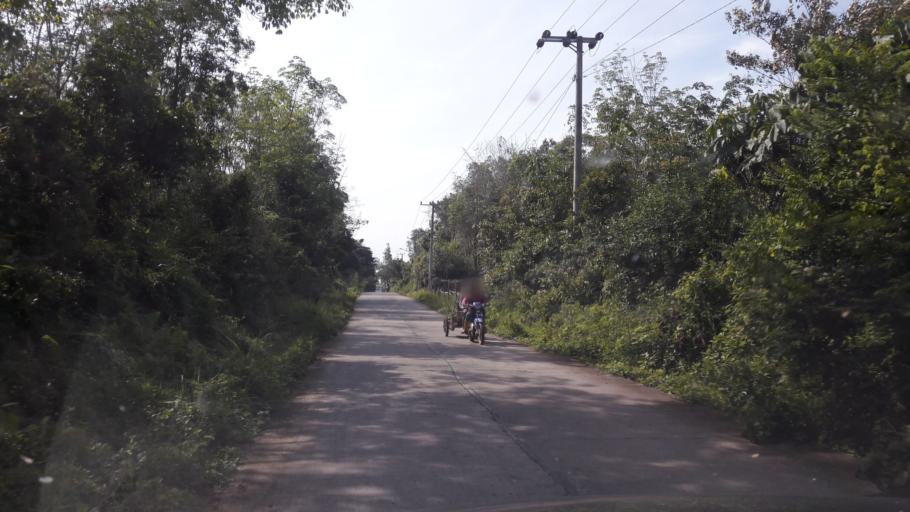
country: ID
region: South Sumatra
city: Gunungmenang
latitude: -3.3311
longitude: 104.0596
